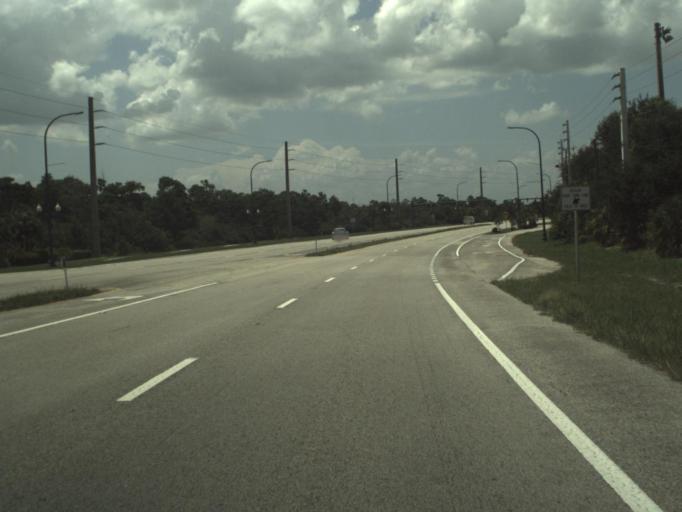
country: US
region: Florida
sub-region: Martin County
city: Hobe Sound
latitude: 27.0541
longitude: -80.1334
